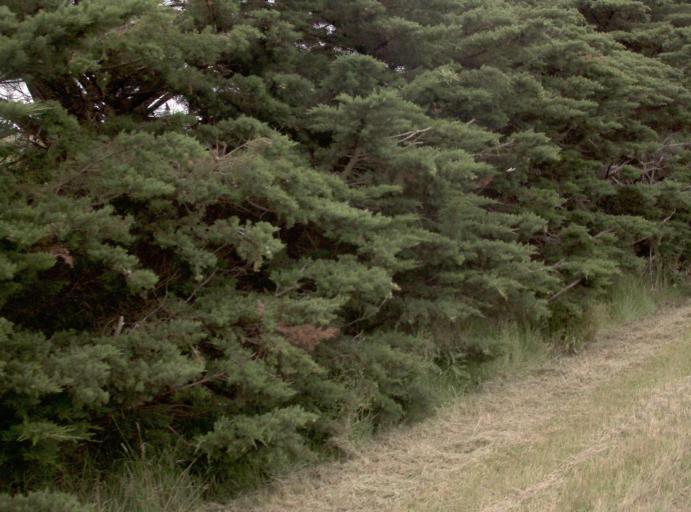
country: AU
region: Victoria
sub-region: Bass Coast
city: North Wonthaggi
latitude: -38.5810
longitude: 145.6275
